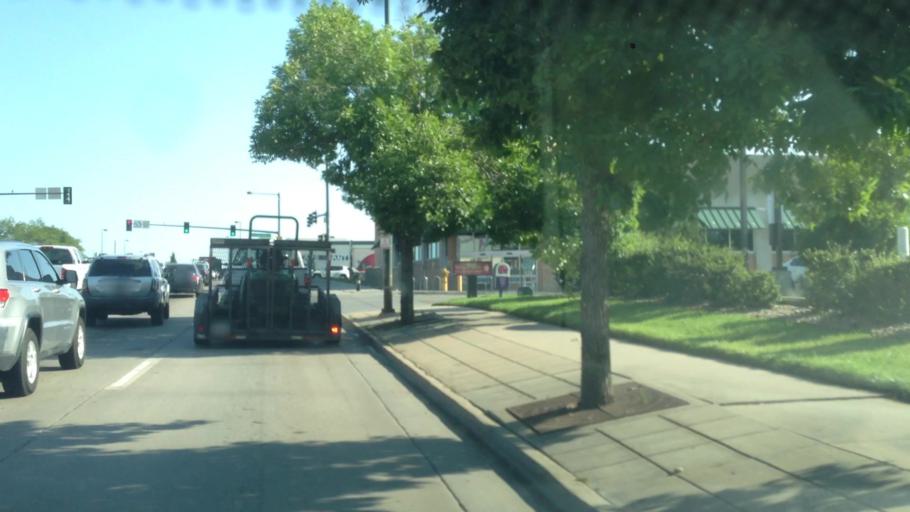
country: US
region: Colorado
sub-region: Denver County
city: Denver
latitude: 39.7103
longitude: -105.0250
